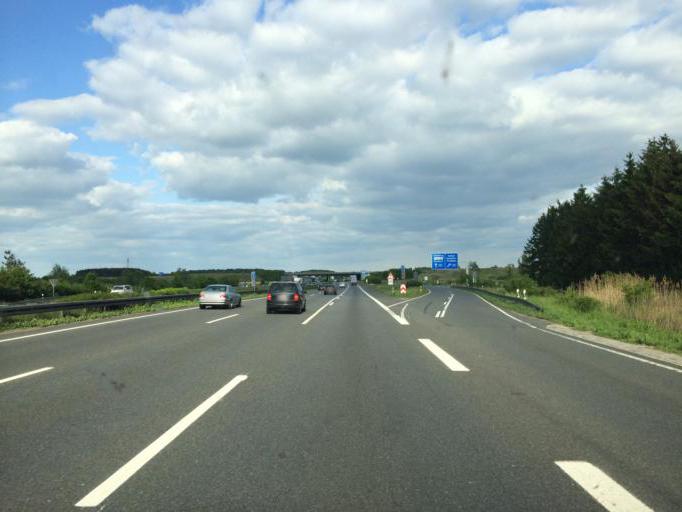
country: DE
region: Lower Saxony
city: Lehre
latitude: 52.3081
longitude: 10.7192
